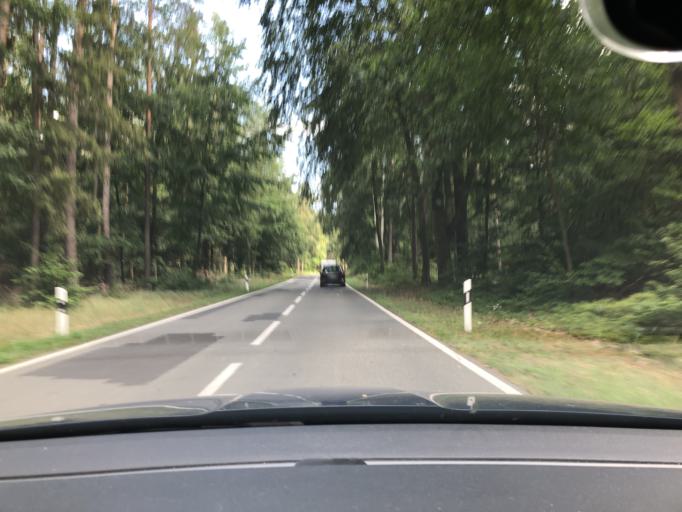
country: DE
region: Brandenburg
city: Neuruppin
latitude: 53.0292
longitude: 12.7508
